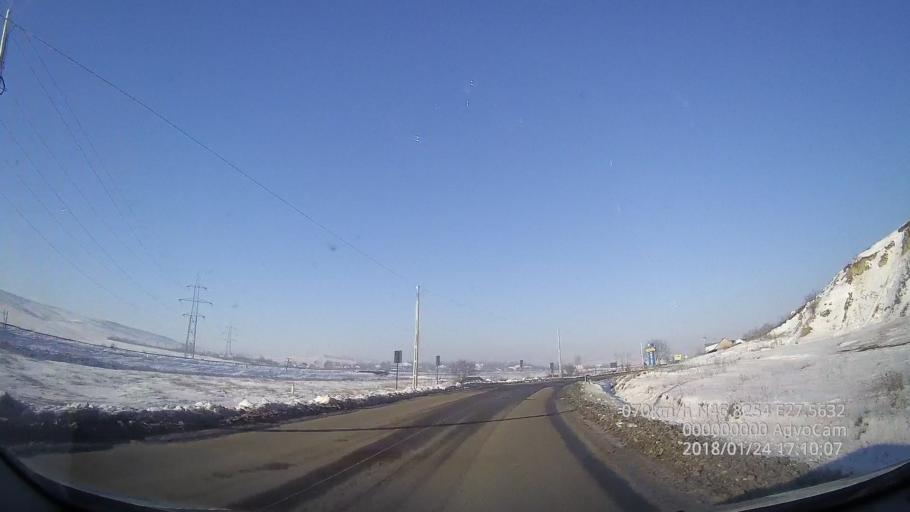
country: RO
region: Vaslui
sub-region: Comuna Vulturesti
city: Vulturesti
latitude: 46.8260
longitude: 27.5632
